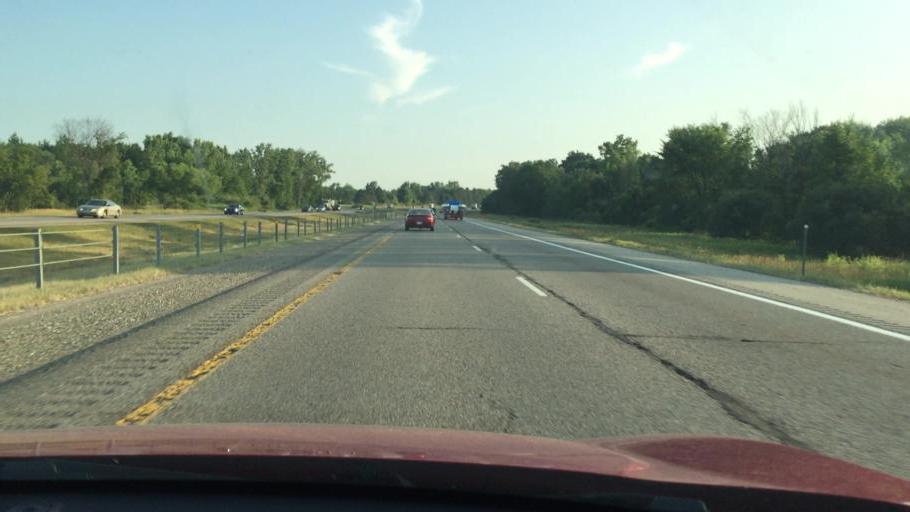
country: US
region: Michigan
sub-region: Livingston County
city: Brighton
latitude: 42.5898
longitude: -83.7393
